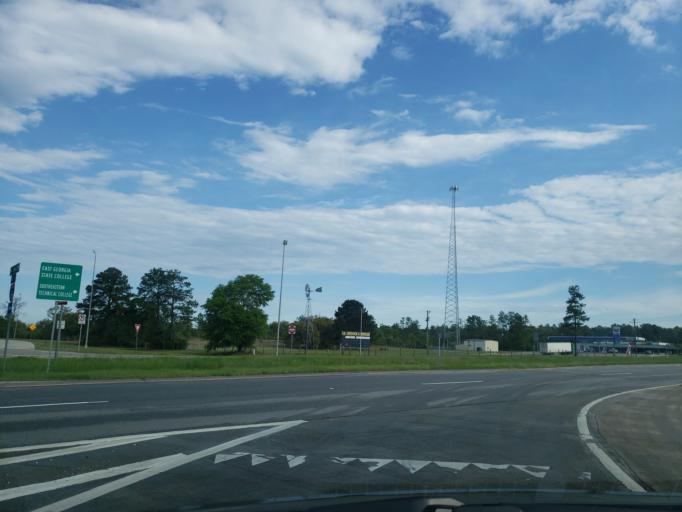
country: US
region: Georgia
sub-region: Emanuel County
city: Swainsboro
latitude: 32.4019
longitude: -82.3068
